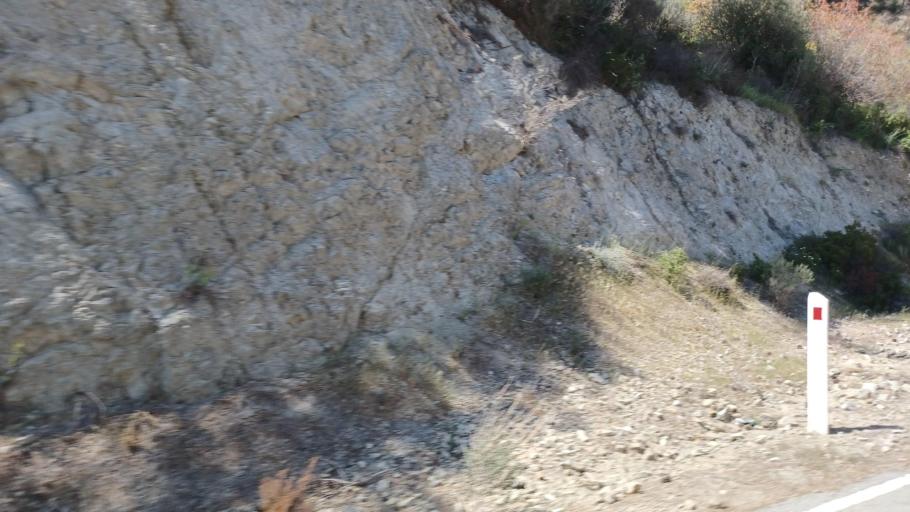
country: CY
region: Limassol
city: Parekklisha
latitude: 34.8059
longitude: 33.1412
